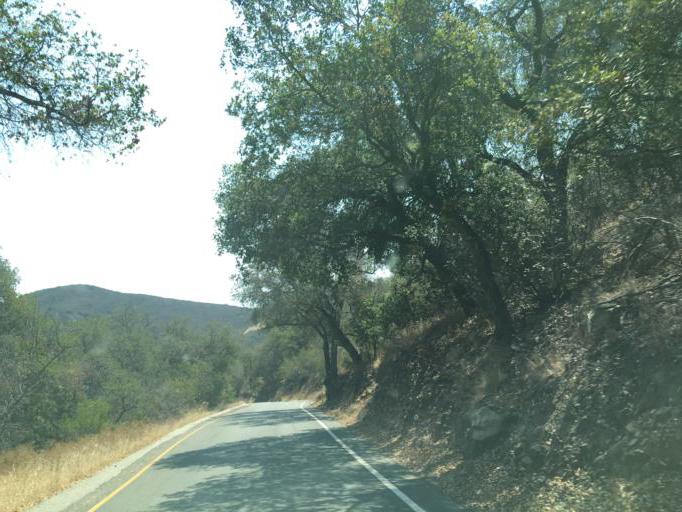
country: US
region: California
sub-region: Los Angeles County
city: Las Flores
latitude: 34.0468
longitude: -118.5938
